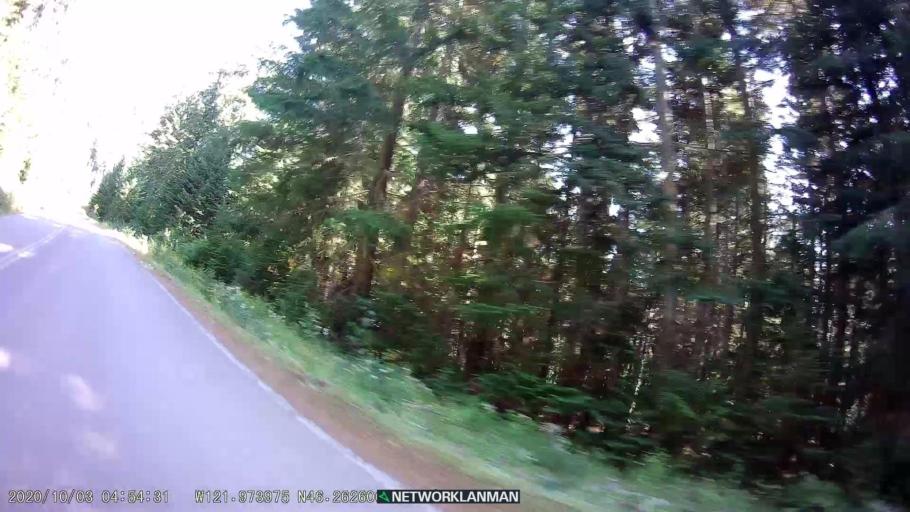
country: US
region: Washington
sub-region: Lewis County
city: Morton
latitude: 46.2627
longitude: -121.9738
